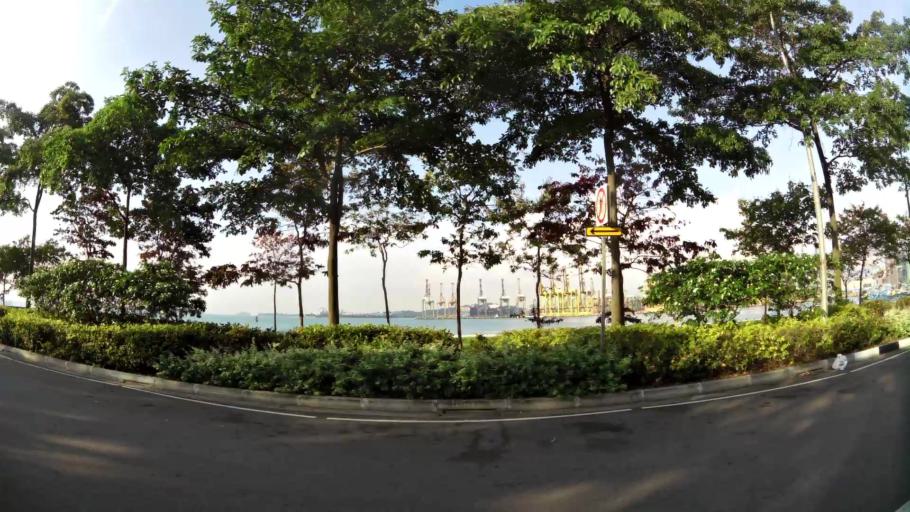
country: SG
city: Singapore
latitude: 1.2679
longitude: 103.8586
